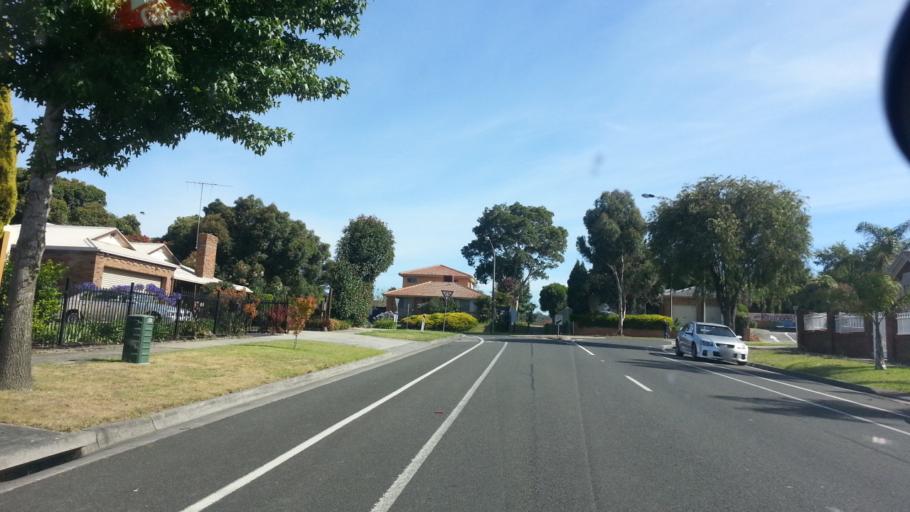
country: AU
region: Victoria
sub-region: Casey
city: Endeavour Hills
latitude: -37.9683
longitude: 145.2745
